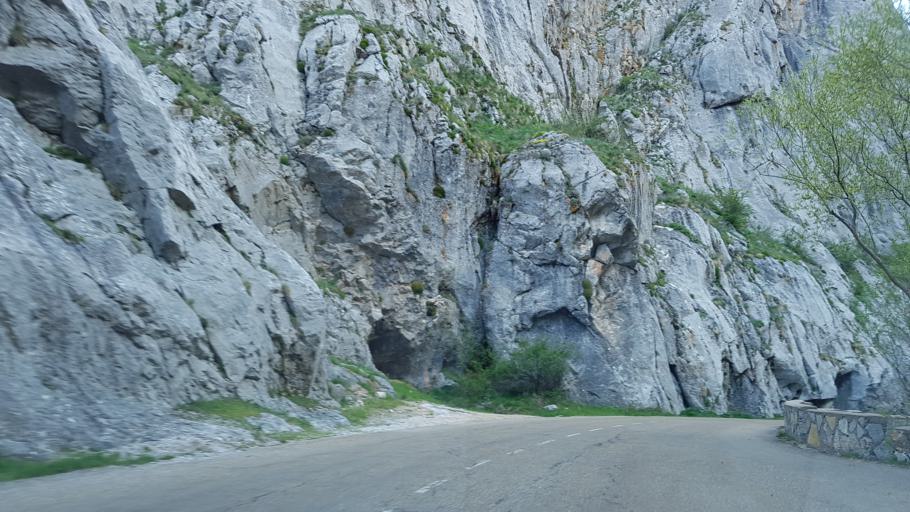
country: ES
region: Castille and Leon
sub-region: Provincia de Leon
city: Vegacervera
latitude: 42.9042
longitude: -5.5394
